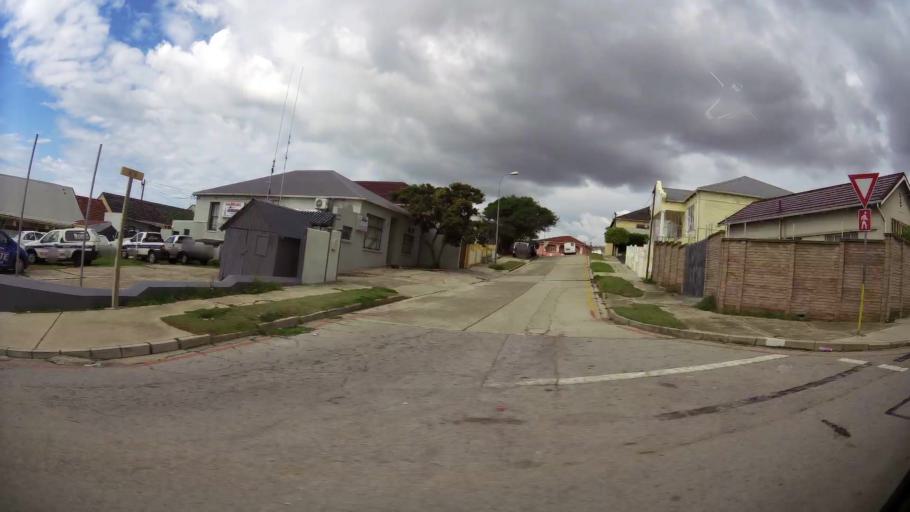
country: ZA
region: Eastern Cape
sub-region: Nelson Mandela Bay Metropolitan Municipality
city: Port Elizabeth
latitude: -33.9485
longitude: 25.6025
